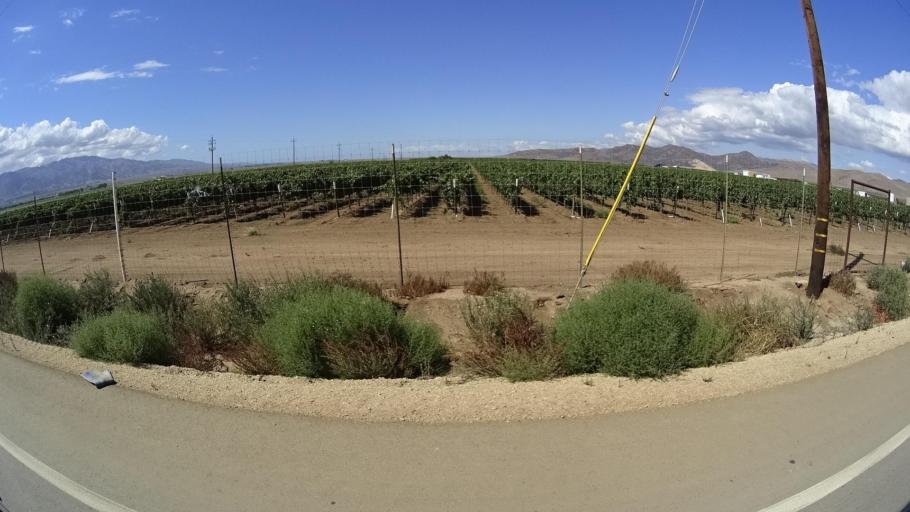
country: US
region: California
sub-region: Monterey County
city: Gonzales
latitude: 36.5262
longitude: -121.4151
